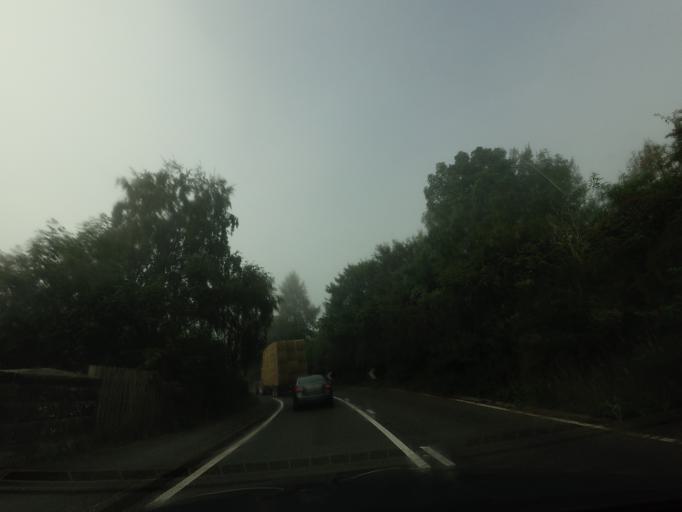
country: GB
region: England
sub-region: Derbyshire
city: Bakewell
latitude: 53.2252
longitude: -1.6724
